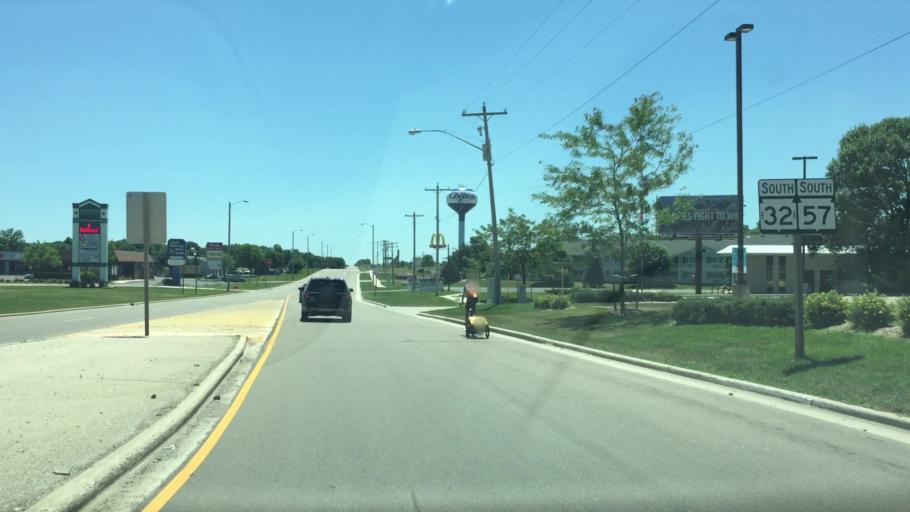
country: US
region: Wisconsin
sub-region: Calumet County
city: Chilton
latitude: 44.0222
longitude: -88.1550
